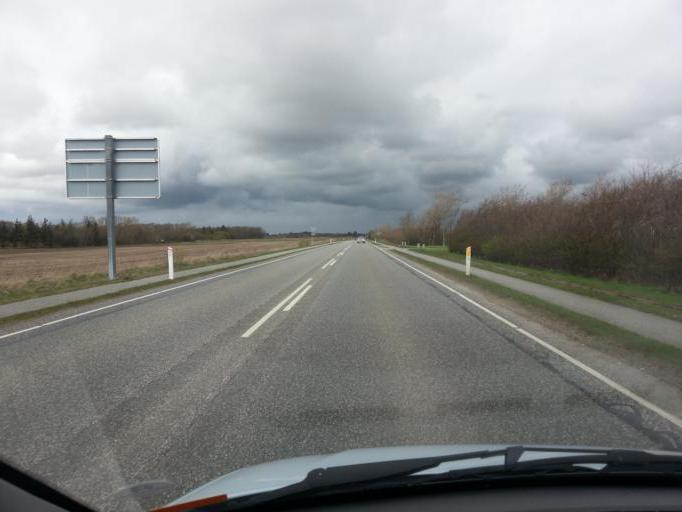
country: DK
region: Central Jutland
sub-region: Ringkobing-Skjern Kommune
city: Ringkobing
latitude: 56.1070
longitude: 8.2608
